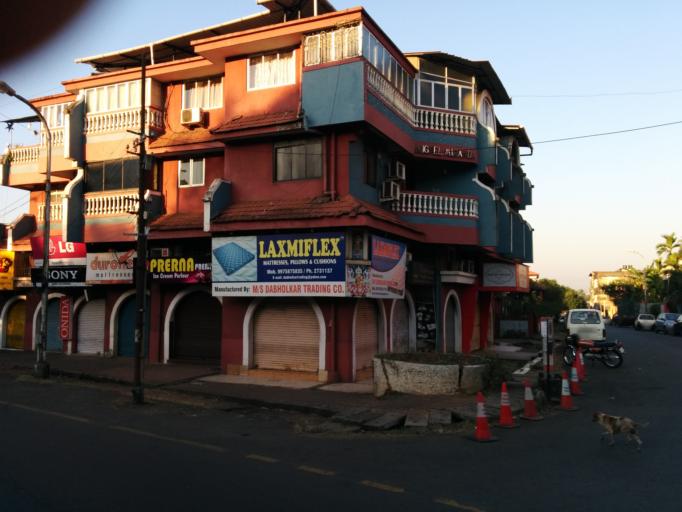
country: IN
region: Goa
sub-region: South Goa
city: Madgaon
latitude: 15.2787
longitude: 73.9596
